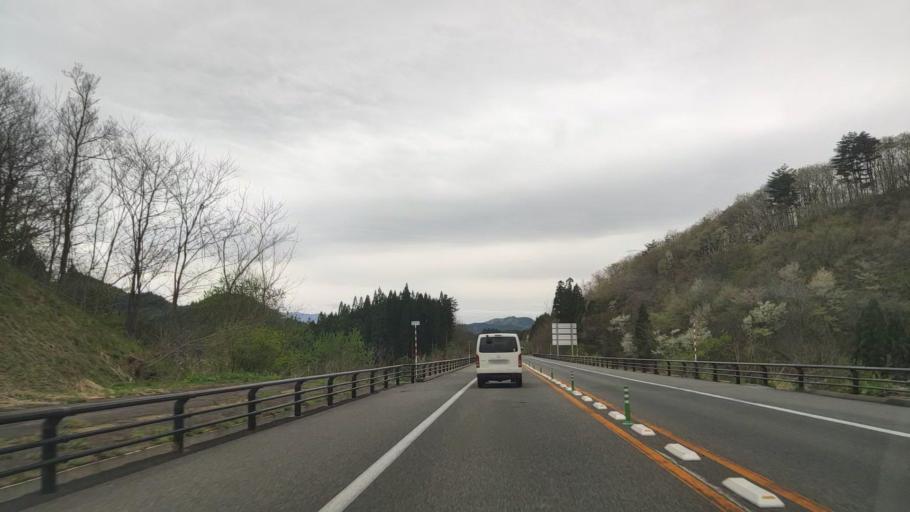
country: JP
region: Akita
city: Odate
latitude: 40.3190
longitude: 140.5896
